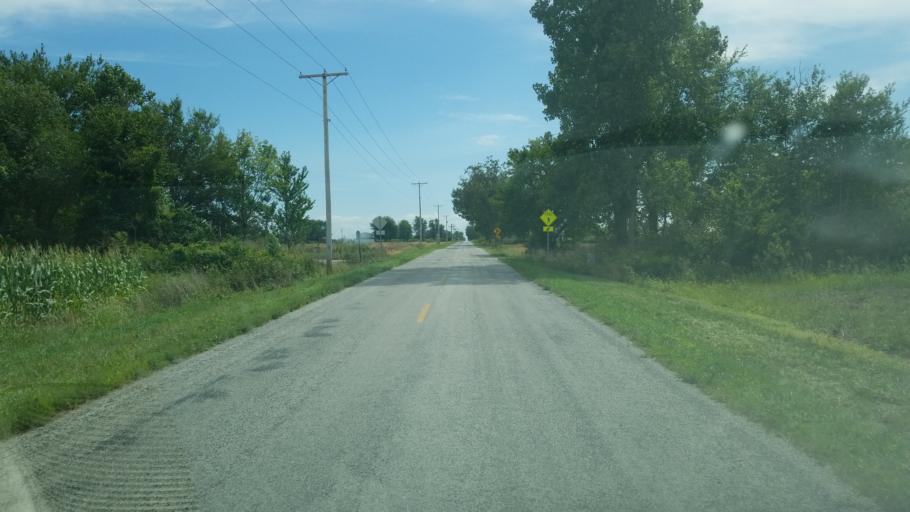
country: US
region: Ohio
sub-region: Union County
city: Richwood
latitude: 40.6031
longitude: -83.3146
